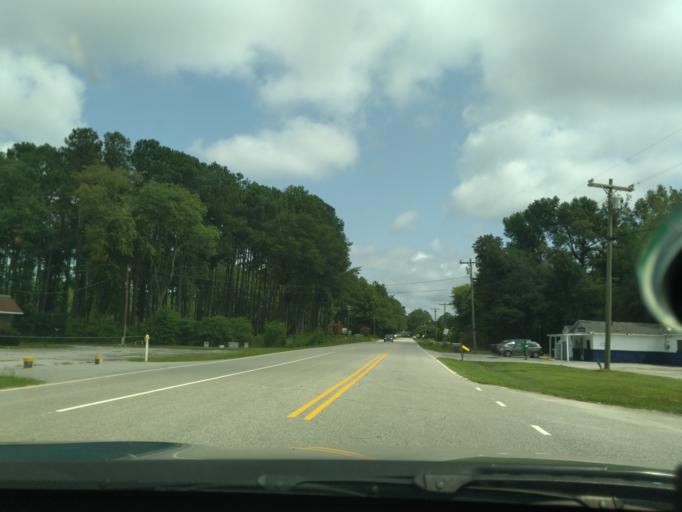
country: US
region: North Carolina
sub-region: Edgecombe County
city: Princeville
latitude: 35.8737
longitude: -77.5229
